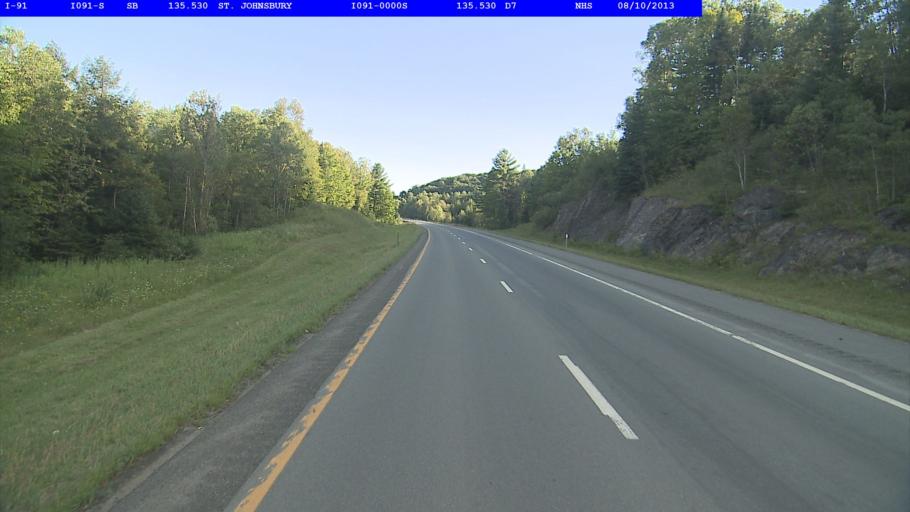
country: US
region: Vermont
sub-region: Caledonia County
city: Lyndon
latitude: 44.4969
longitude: -72.0222
